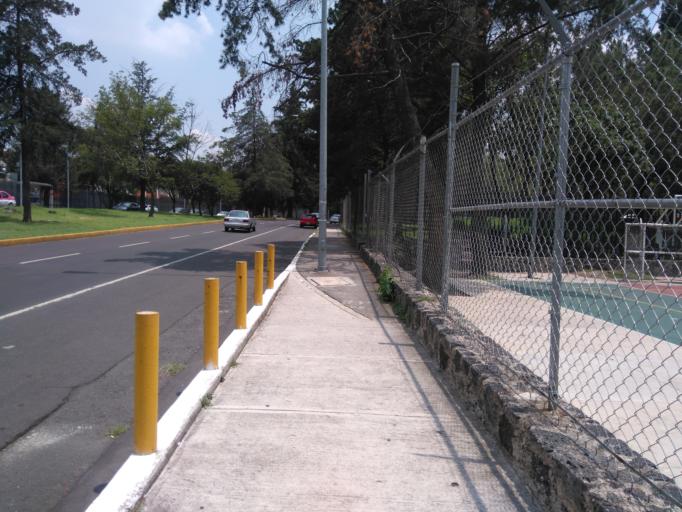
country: MX
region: Mexico City
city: Tlalpan
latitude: 19.3194
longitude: -99.1763
